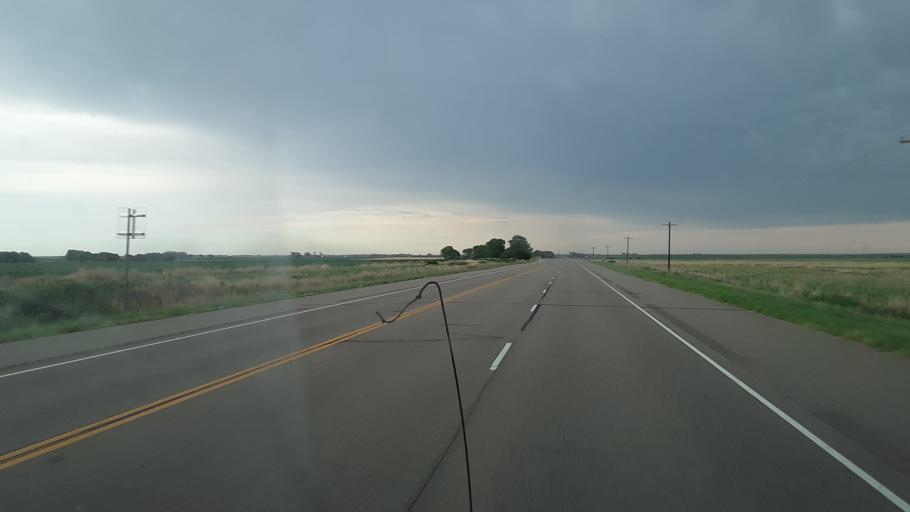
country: US
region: Colorado
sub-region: Bent County
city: Las Animas
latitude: 38.1141
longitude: -102.9473
